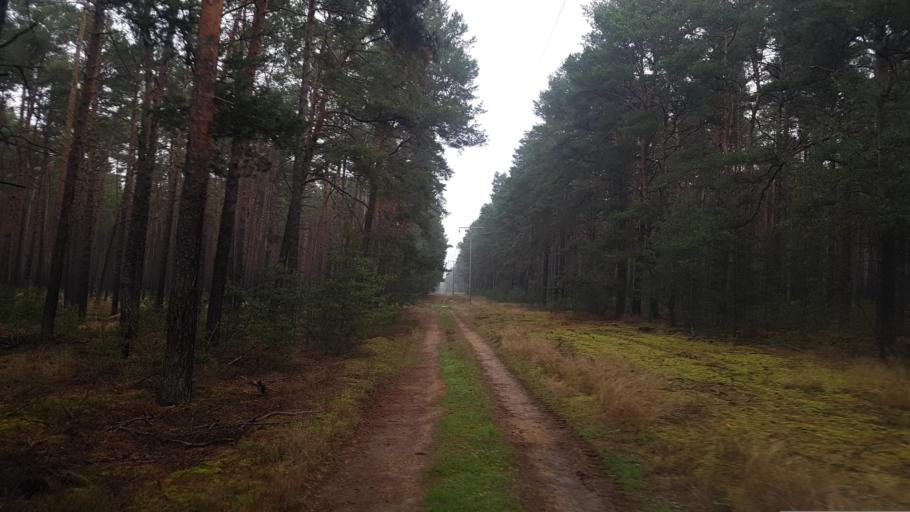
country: DE
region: Brandenburg
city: Crinitz
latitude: 51.6519
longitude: 13.7902
